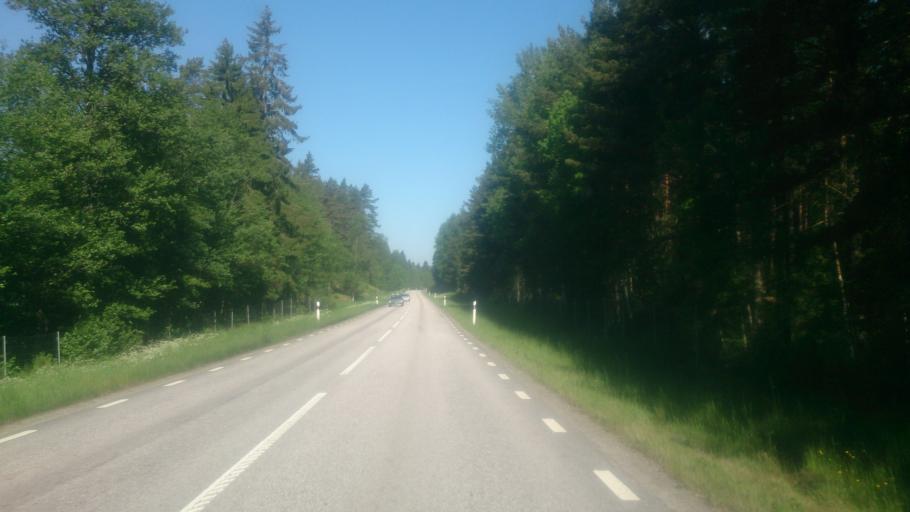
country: SE
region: OEstergoetland
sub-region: Atvidabergs Kommun
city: Atvidaberg
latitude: 58.1674
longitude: 16.0485
